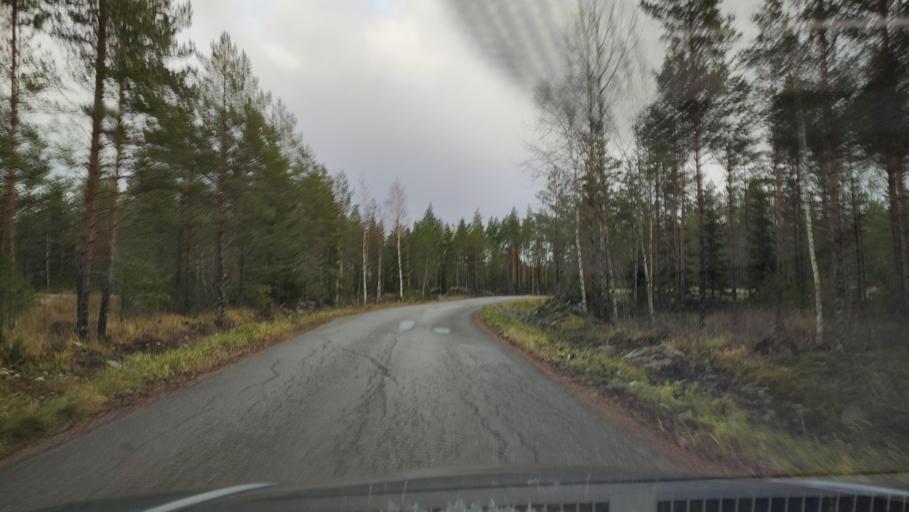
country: FI
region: Ostrobothnia
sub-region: Sydosterbotten
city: Kristinestad
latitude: 62.1496
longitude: 21.5513
